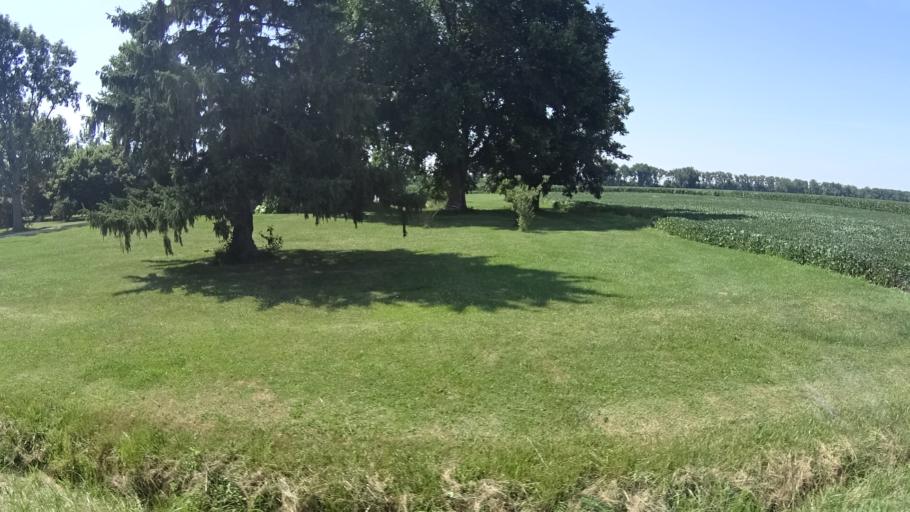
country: US
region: Ohio
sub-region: Erie County
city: Sandusky
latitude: 41.4298
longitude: -82.7907
